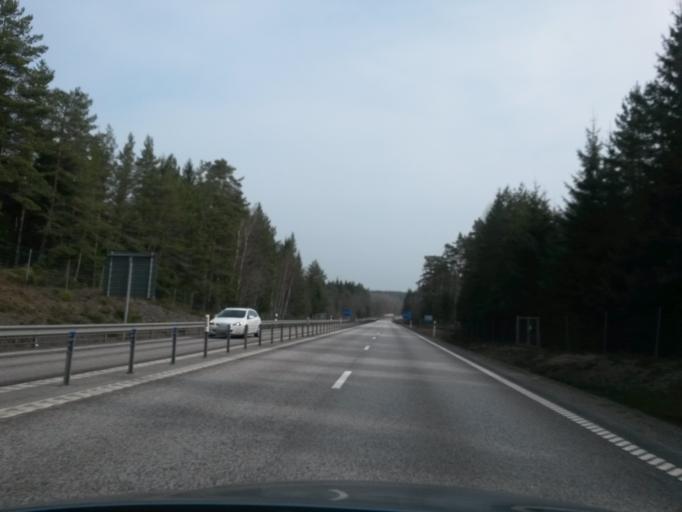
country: SE
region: Vaestra Goetaland
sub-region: Gullspangs Kommun
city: Anderstorp
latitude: 58.8895
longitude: 14.3107
